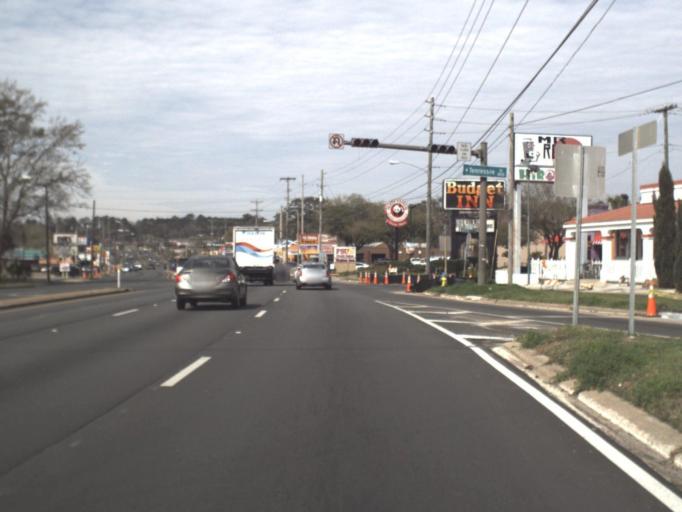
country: US
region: Florida
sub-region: Leon County
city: Tallahassee
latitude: 30.4490
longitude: -84.3043
